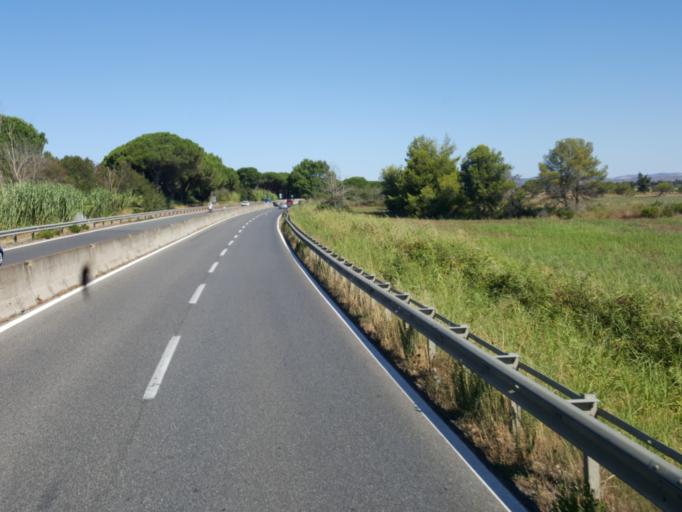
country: IT
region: Tuscany
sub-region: Provincia di Grosseto
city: Albinia
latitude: 42.5113
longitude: 11.1959
